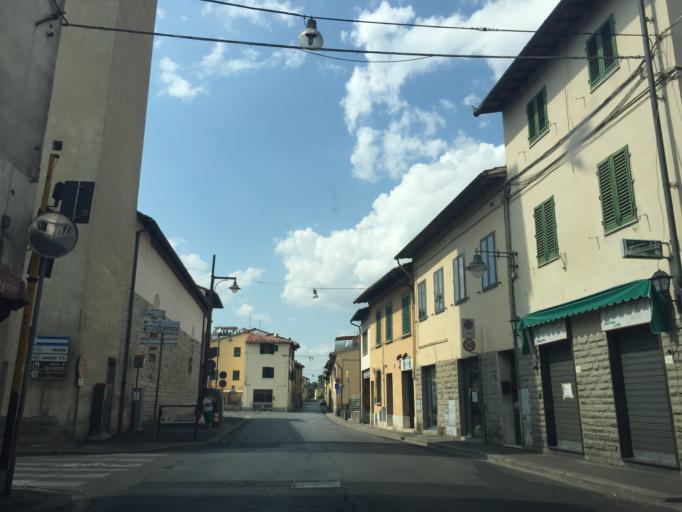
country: IT
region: Tuscany
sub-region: Province of Florence
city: San Donnino
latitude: 43.7953
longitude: 11.1510
